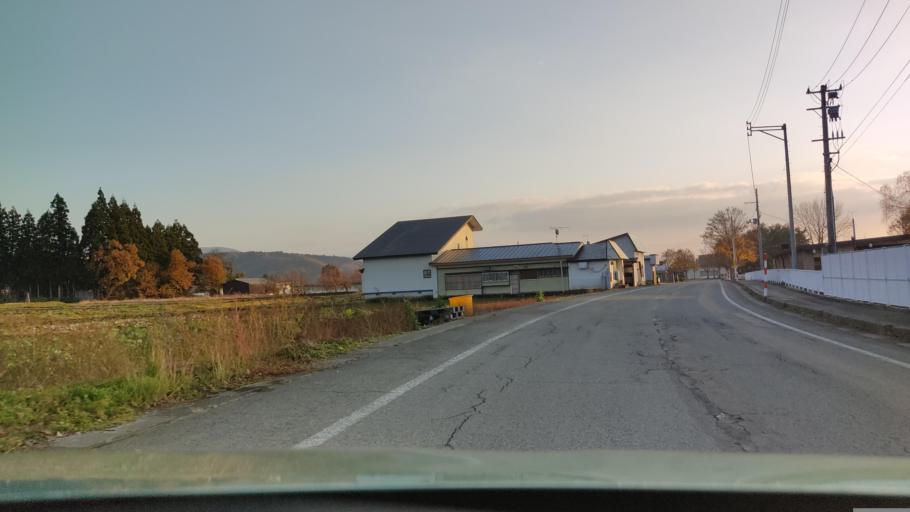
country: JP
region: Akita
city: Omagari
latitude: 39.4653
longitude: 140.5841
